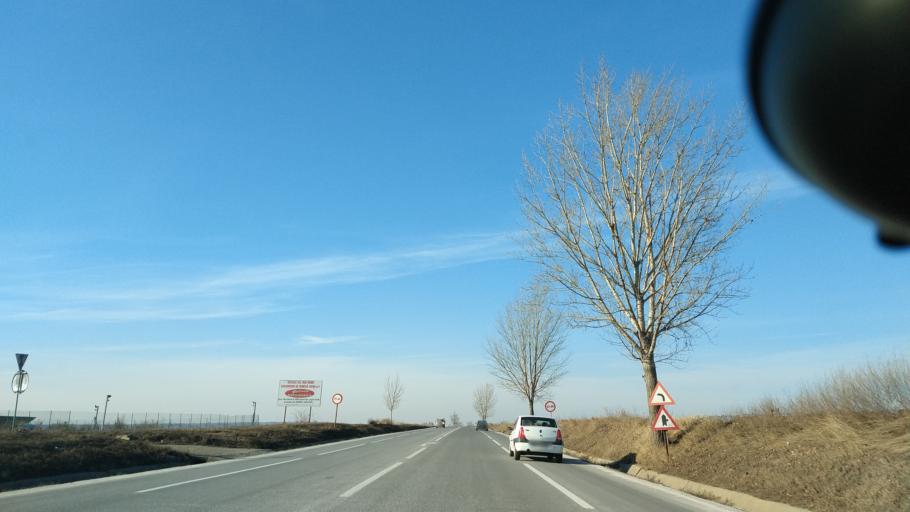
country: RO
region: Iasi
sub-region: Comuna Podu Iloaiei
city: Budai
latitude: 47.2228
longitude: 27.1959
